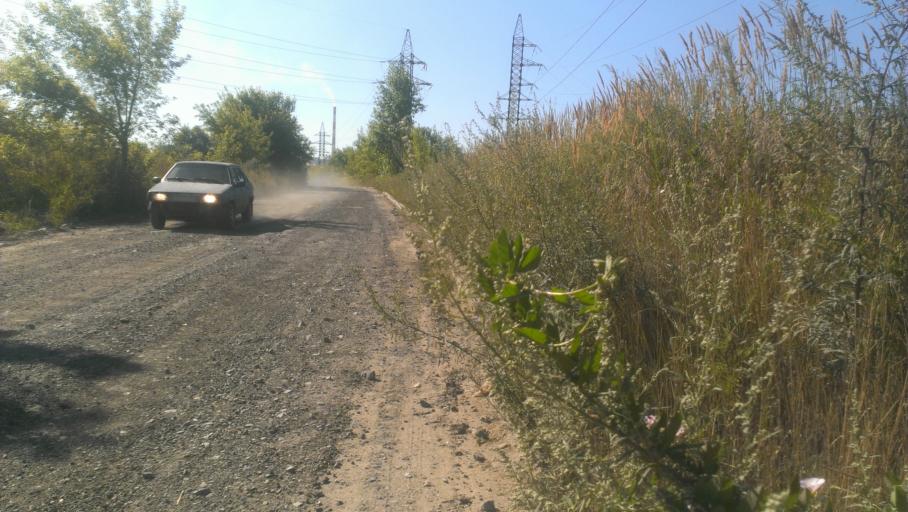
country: RU
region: Altai Krai
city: Novosilikatnyy
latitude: 53.3273
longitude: 83.6462
